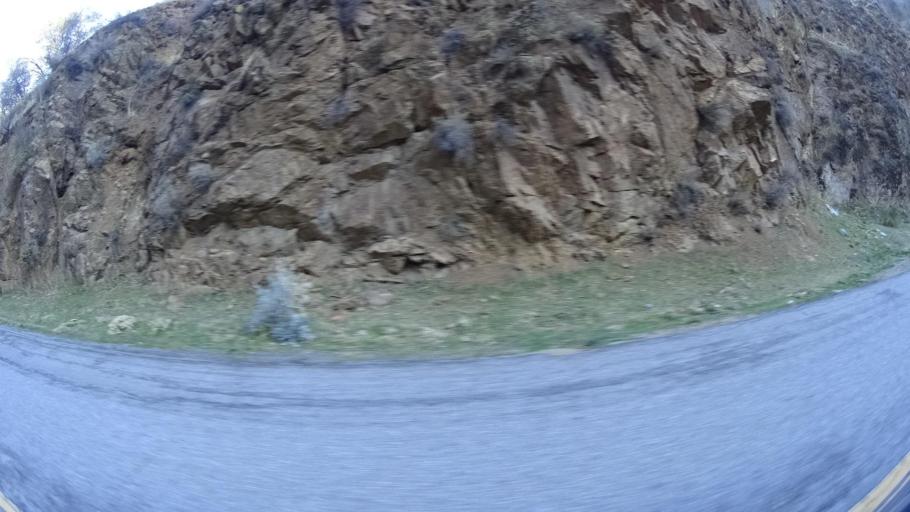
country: US
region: California
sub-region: Kern County
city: Golden Hills
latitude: 35.3135
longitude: -118.5297
